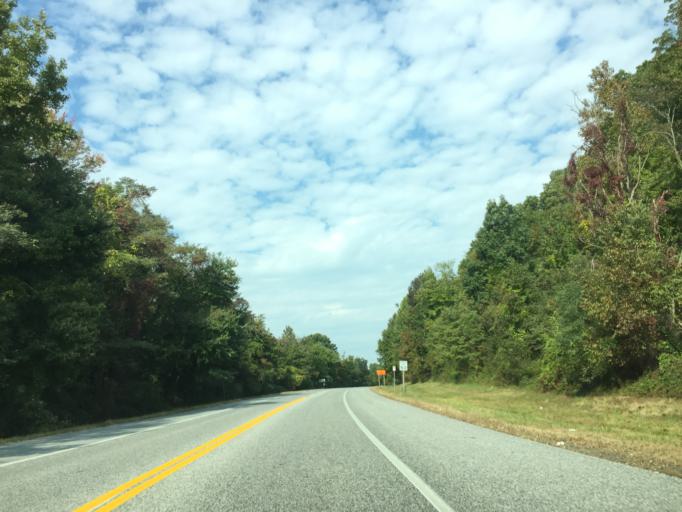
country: US
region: Maryland
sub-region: Harford County
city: Edgewood
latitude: 39.4186
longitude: -76.3085
